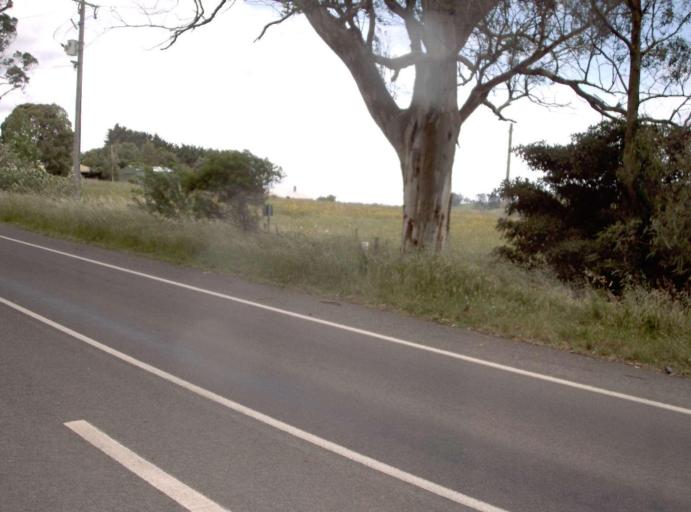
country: AU
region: Victoria
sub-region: Baw Baw
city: Warragul
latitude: -38.1128
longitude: 145.8410
